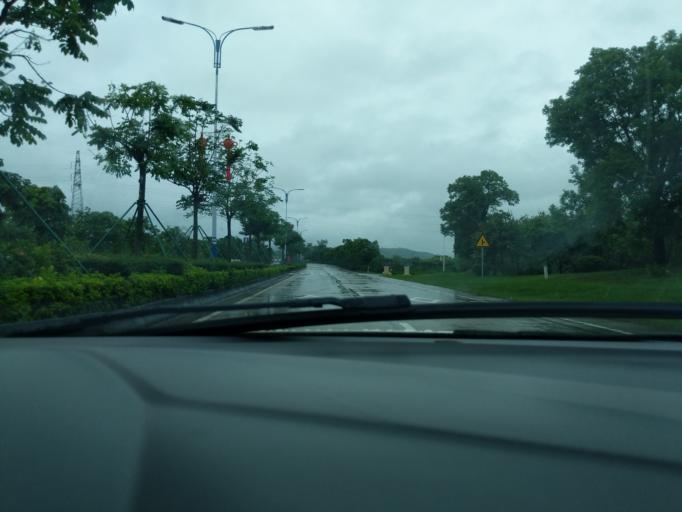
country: CN
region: Guangdong
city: Pingshi
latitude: 22.2215
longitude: 112.3169
